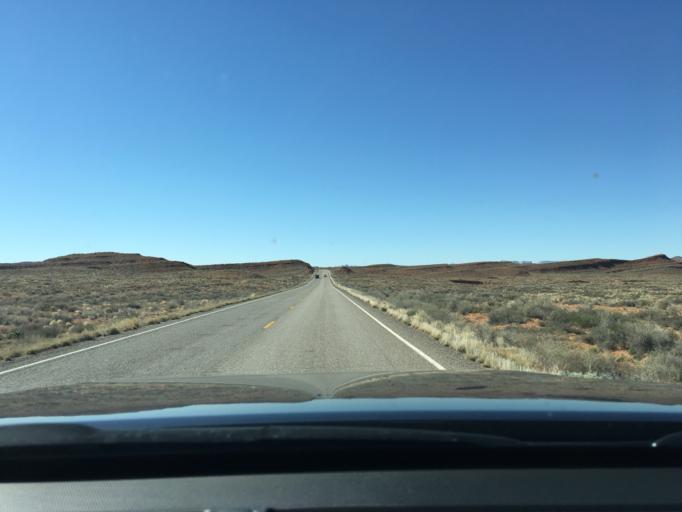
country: US
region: Utah
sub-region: San Juan County
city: Blanding
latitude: 37.1735
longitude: -109.8601
